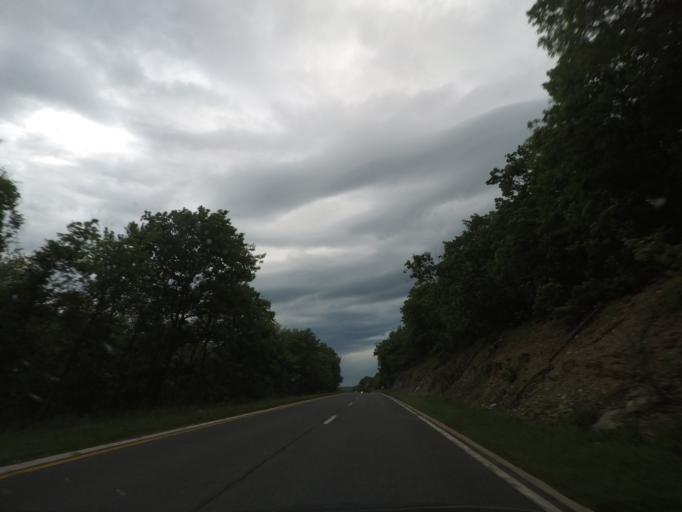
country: US
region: New York
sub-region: Dutchess County
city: Pine Plains
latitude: 42.0999
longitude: -73.7180
